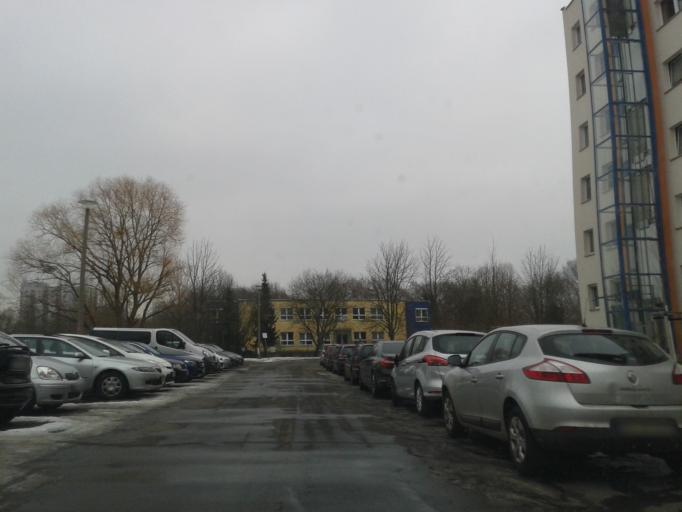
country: DE
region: Saxony
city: Dresden
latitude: 51.0219
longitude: 13.7359
